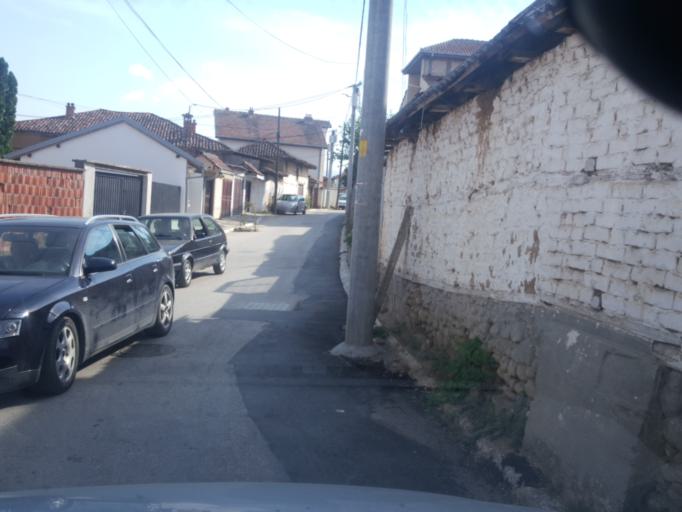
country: XK
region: Gjakova
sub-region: Komuna e Gjakoves
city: Gjakove
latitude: 42.3837
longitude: 20.4232
